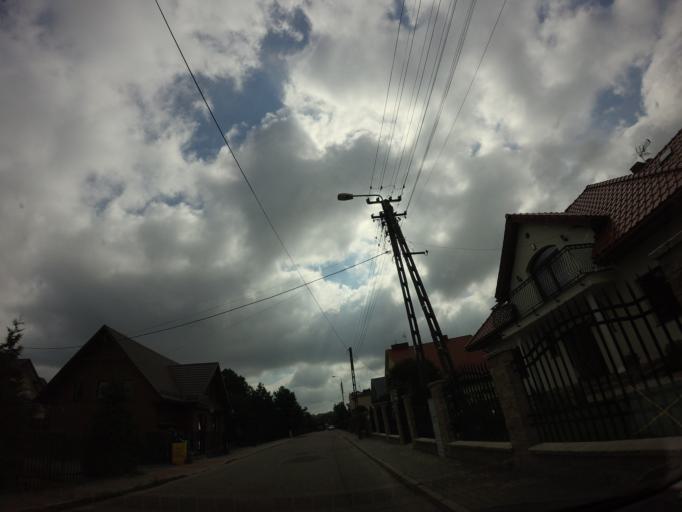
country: PL
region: Podlasie
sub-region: Bialystok
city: Bialystok
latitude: 53.1229
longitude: 23.2314
